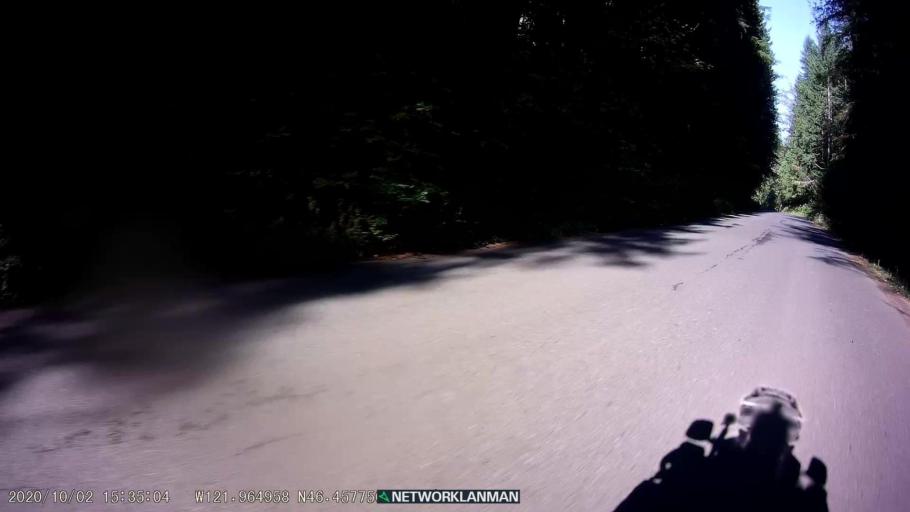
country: US
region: Washington
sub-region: Lewis County
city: Morton
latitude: 46.4580
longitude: -121.9646
